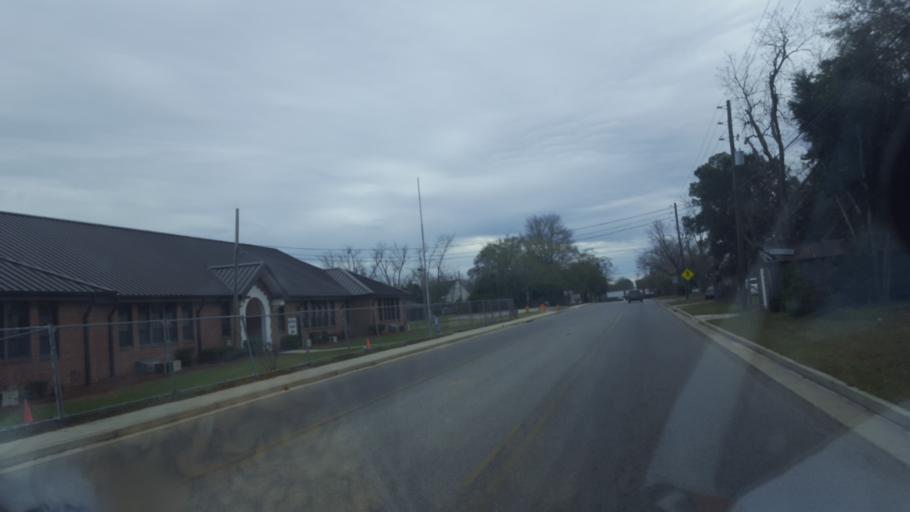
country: US
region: Georgia
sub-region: Ben Hill County
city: Fitzgerald
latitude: 31.7193
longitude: -83.2599
